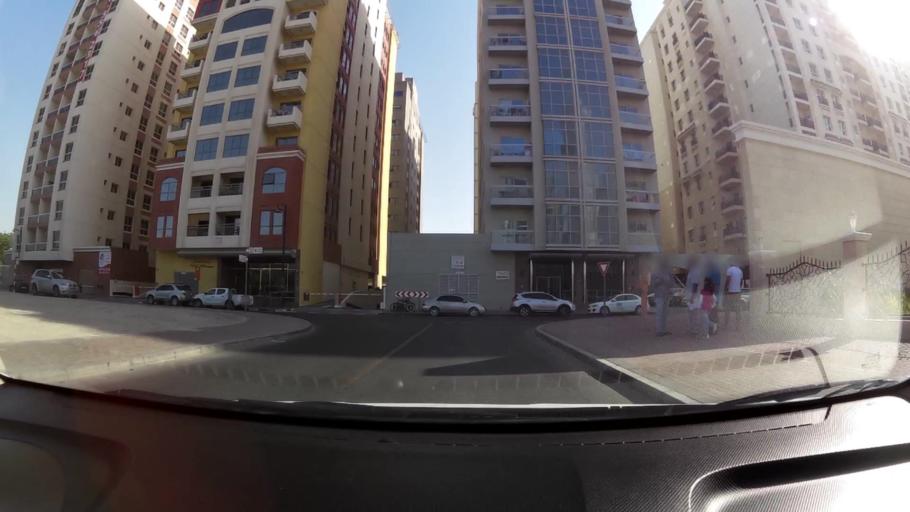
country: AE
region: Ash Shariqah
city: Sharjah
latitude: 25.2900
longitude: 55.3799
